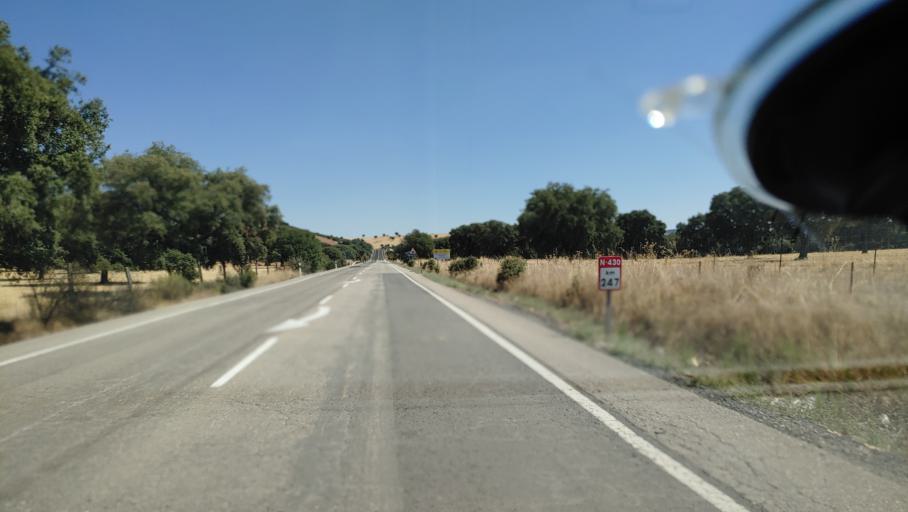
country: ES
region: Castille-La Mancha
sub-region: Provincia de Ciudad Real
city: Saceruela
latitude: 39.0166
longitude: -4.4745
